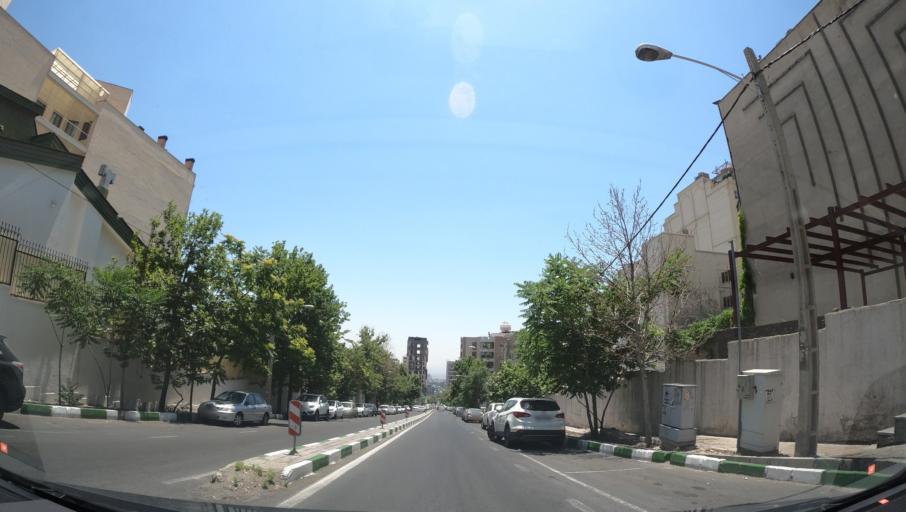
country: IR
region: Tehran
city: Tajrish
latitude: 35.8095
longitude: 51.4003
